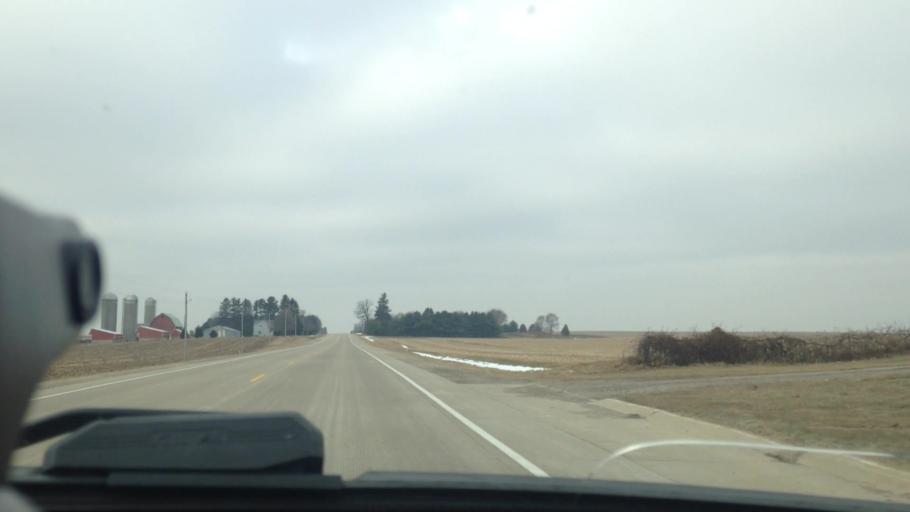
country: US
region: Wisconsin
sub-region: Dodge County
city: Juneau
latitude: 43.4735
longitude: -88.7090
